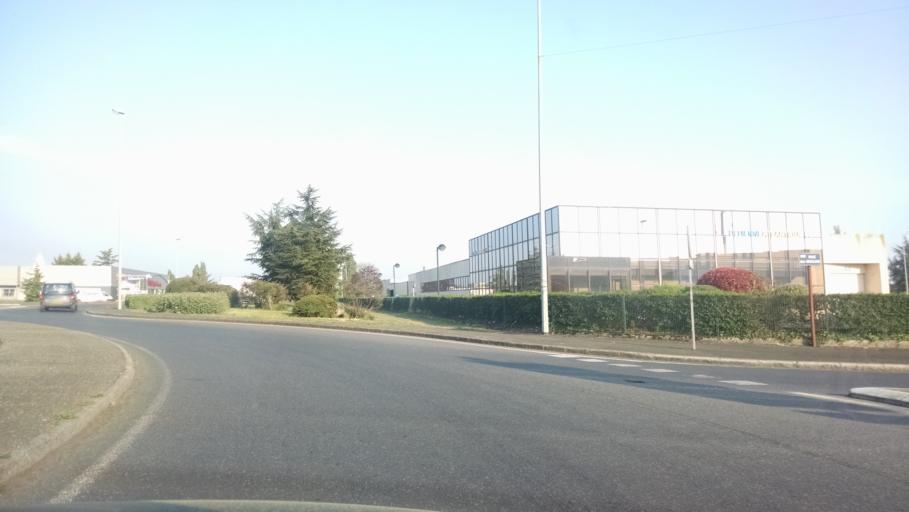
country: FR
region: Pays de la Loire
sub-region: Departement de la Loire-Atlantique
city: Getigne
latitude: 47.0834
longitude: -1.2581
